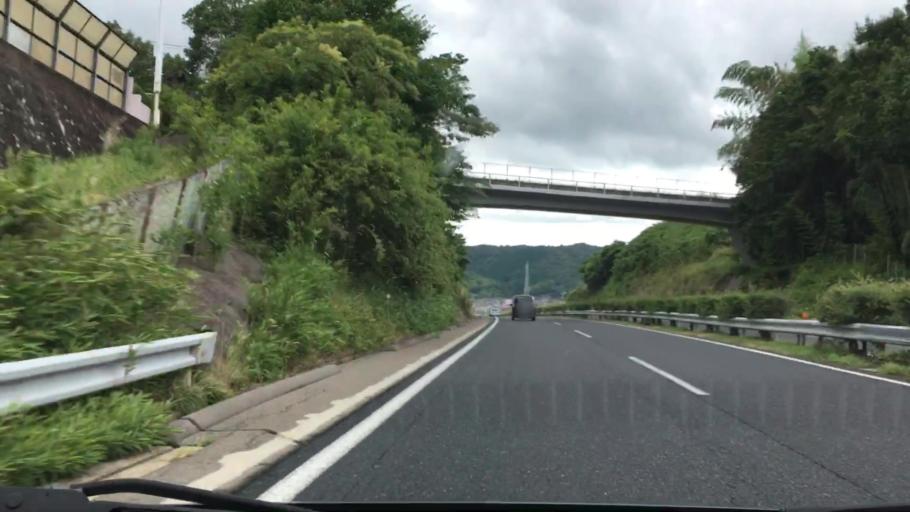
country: JP
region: Okayama
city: Tsuyama
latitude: 35.0778
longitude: 134.0141
